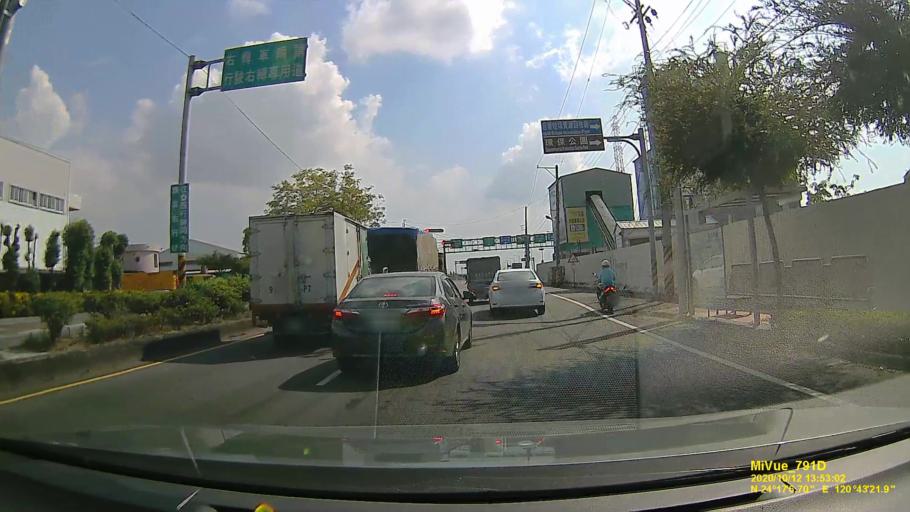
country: TW
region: Taiwan
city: Fengyuan
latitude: 24.2851
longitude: 120.7227
